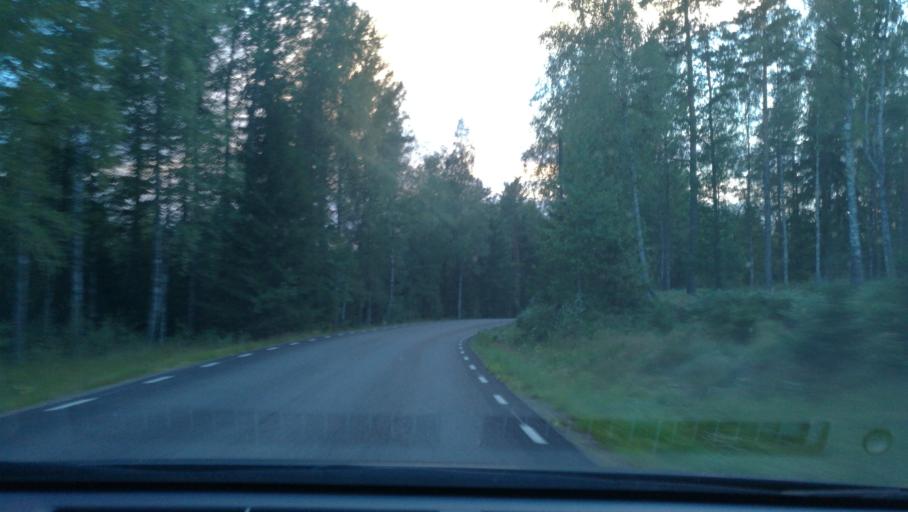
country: SE
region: OEstergoetland
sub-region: Norrkopings Kommun
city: Jursla
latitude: 58.8113
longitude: 16.0928
